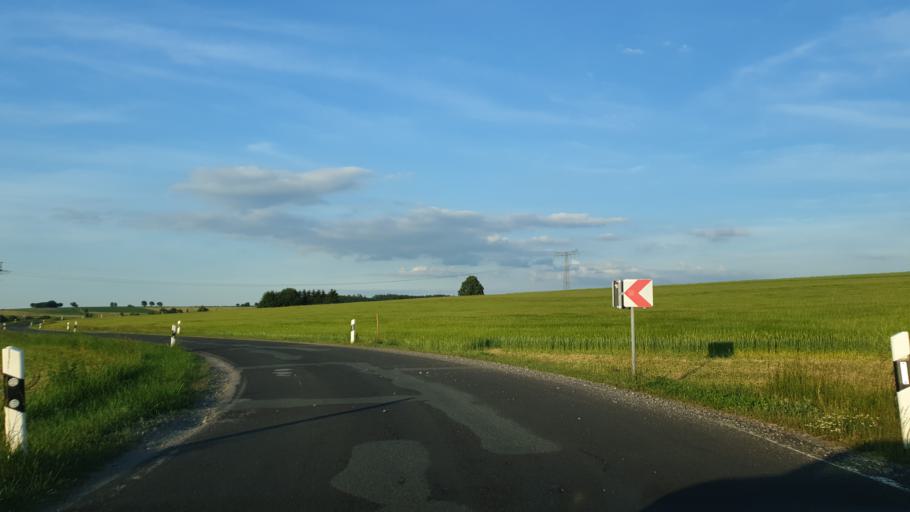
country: DE
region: Saxony
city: Hartenstein
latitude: 50.6610
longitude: 12.7107
